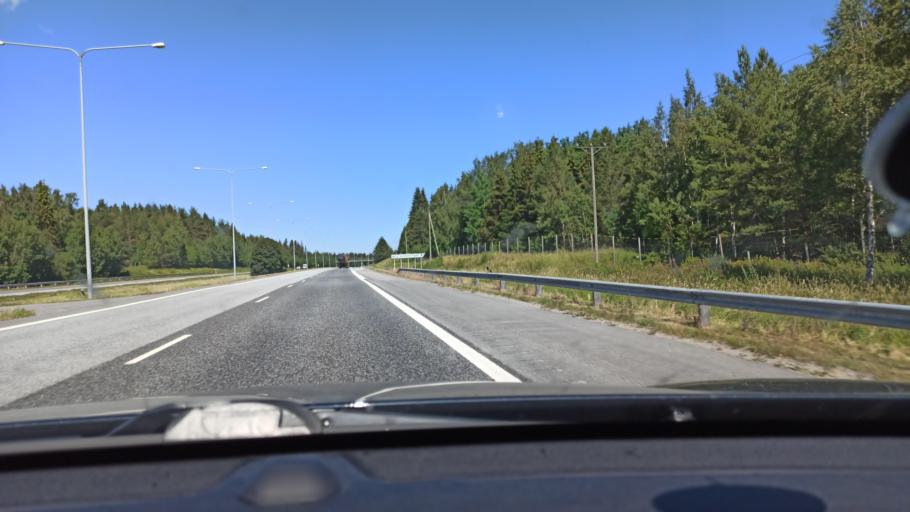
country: FI
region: Ostrobothnia
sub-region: Vaasa
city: Ristinummi
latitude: 63.0483
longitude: 21.7205
